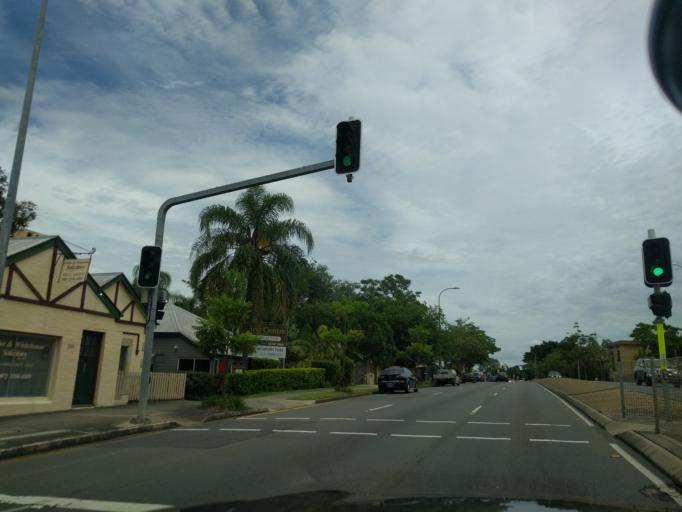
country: AU
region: Queensland
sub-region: Brisbane
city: Wilston
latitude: -27.4343
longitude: 153.0059
